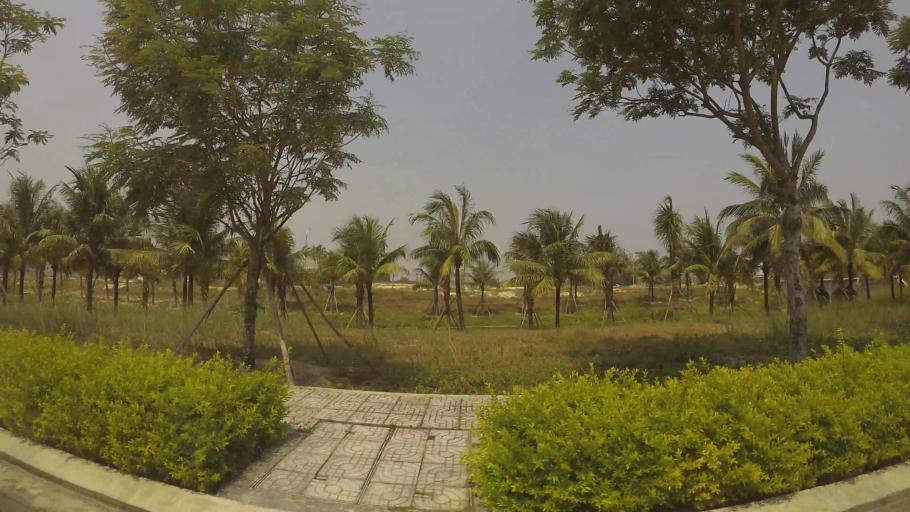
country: VN
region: Da Nang
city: Ngu Hanh Son
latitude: 15.9732
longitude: 108.2639
